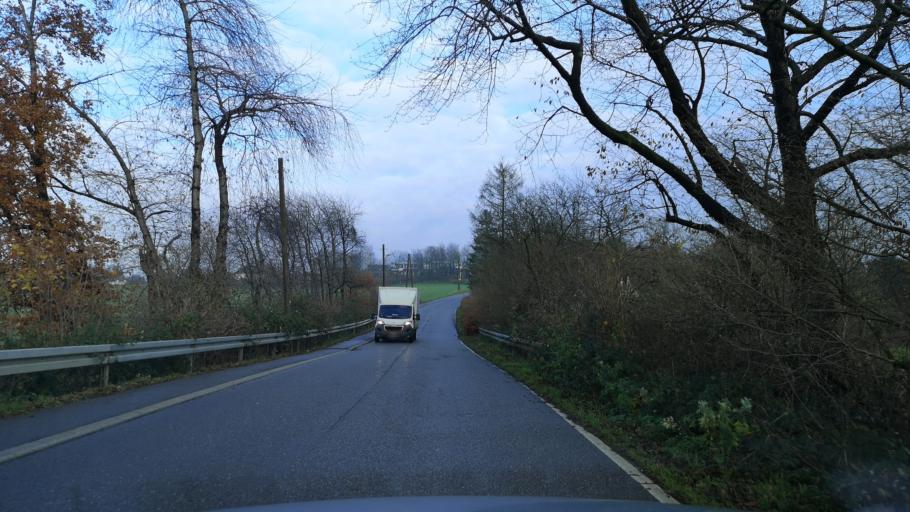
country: DE
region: North Rhine-Westphalia
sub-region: Regierungsbezirk Dusseldorf
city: Velbert
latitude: 51.3705
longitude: 7.0092
